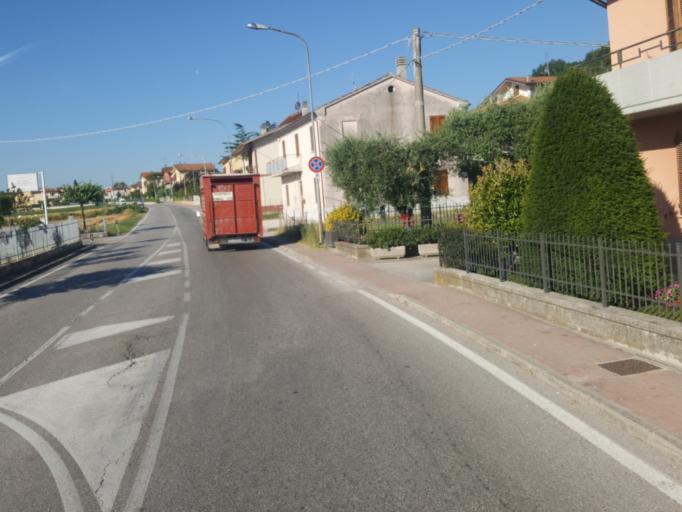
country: IT
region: The Marches
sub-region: Provincia di Pesaro e Urbino
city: Borgo Massano
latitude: 43.8221
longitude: 12.6687
